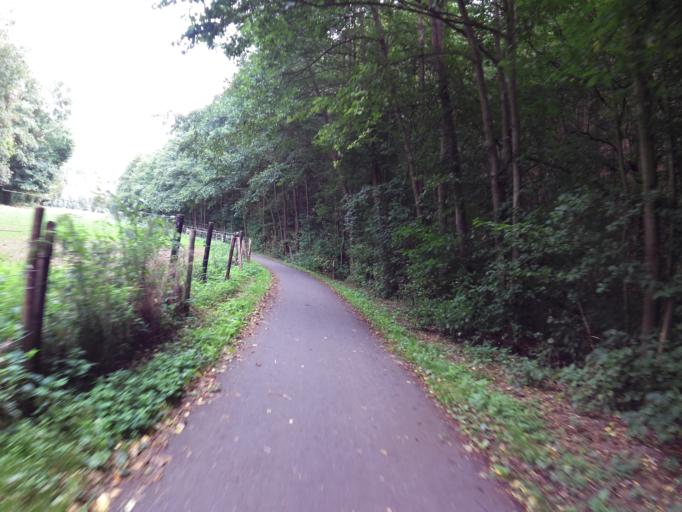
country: DE
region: North Rhine-Westphalia
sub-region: Regierungsbezirk Koln
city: Nideggen
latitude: 50.6997
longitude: 6.4501
